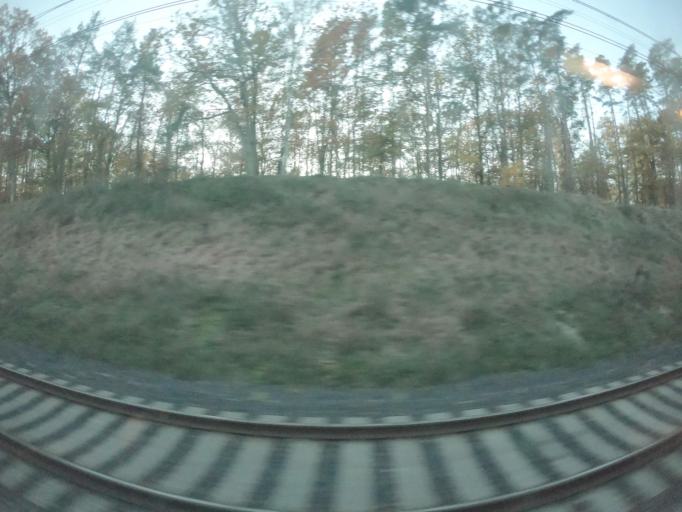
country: PL
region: West Pomeranian Voivodeship
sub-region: Powiat mysliborski
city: Boleszkowice
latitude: 52.7209
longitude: 14.5285
